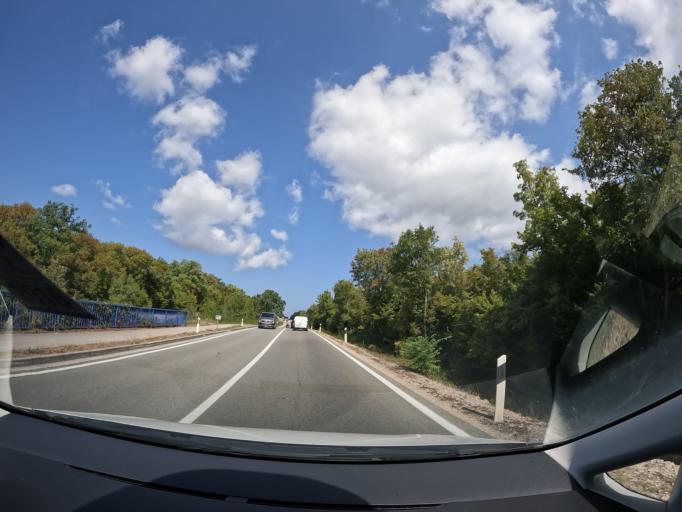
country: HR
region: Primorsko-Goranska
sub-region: Grad Krk
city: Krk
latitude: 45.0856
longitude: 14.5433
